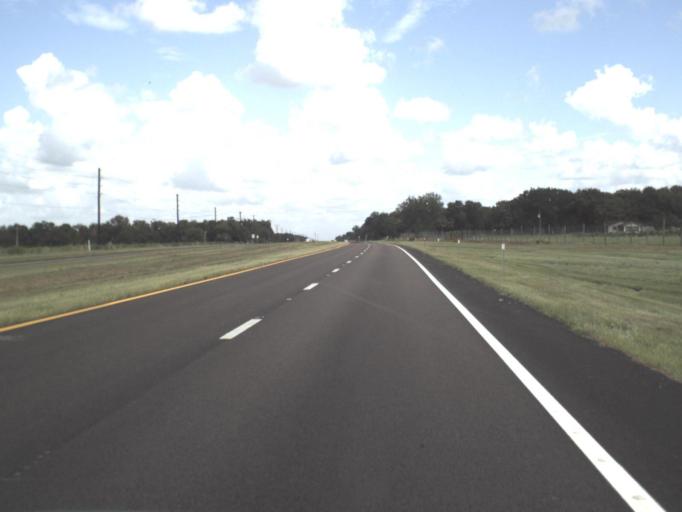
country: US
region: Florida
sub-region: Hardee County
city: Zolfo Springs
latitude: 27.4080
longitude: -81.7952
